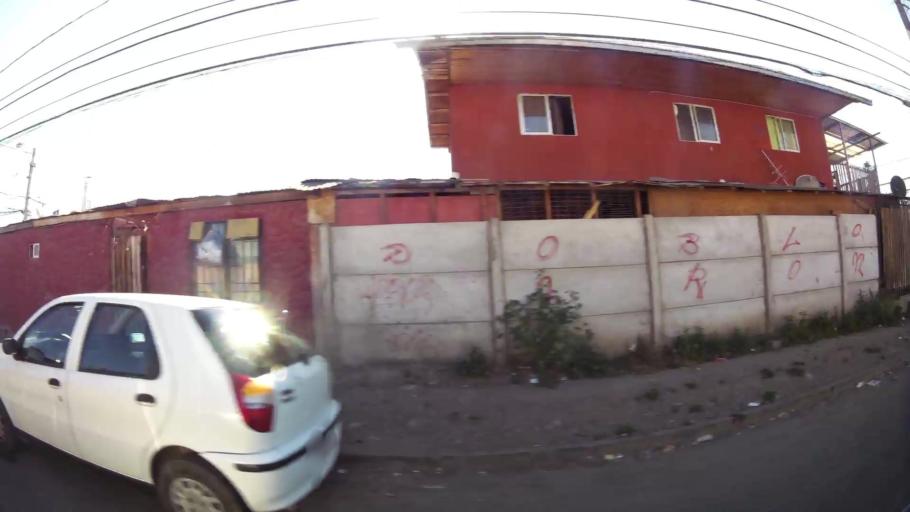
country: CL
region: Santiago Metropolitan
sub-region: Provincia de Talagante
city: Penaflor
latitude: -33.6084
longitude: -70.8716
